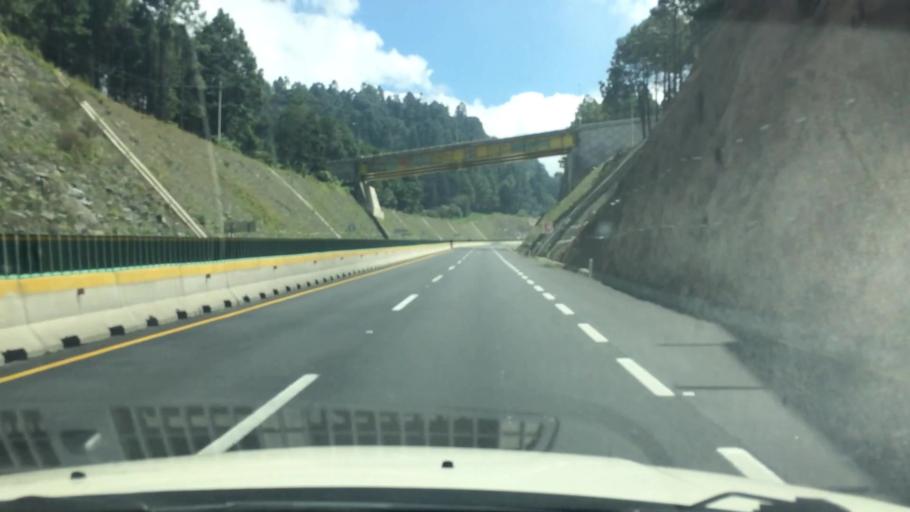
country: MX
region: Morelos
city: San Jeronimo Acazulco
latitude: 19.2978
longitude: -99.4040
